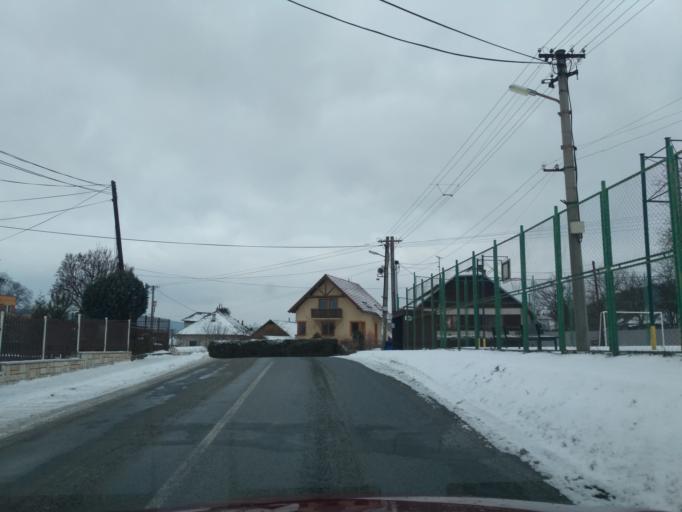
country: SK
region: Presovsky
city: Sabinov
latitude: 49.0097
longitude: 21.1265
